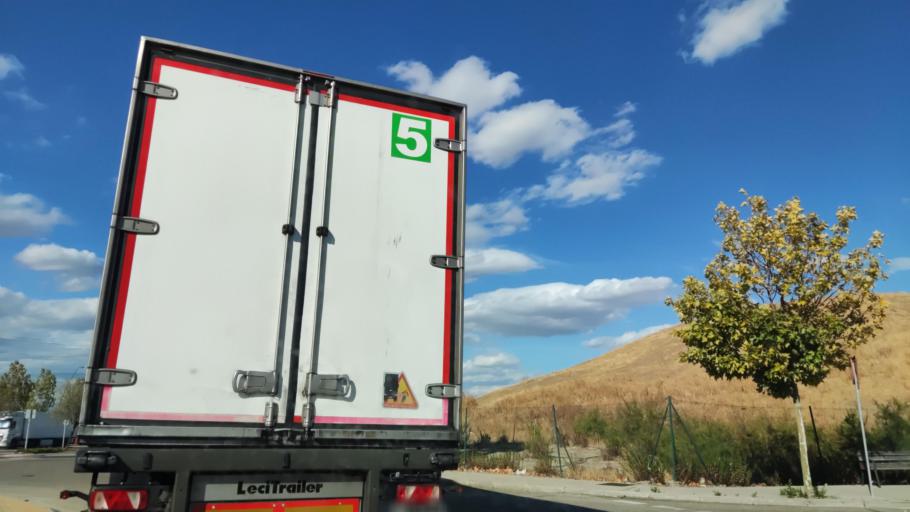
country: ES
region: Madrid
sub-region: Provincia de Madrid
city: Pinto
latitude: 40.2827
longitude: -3.6794
